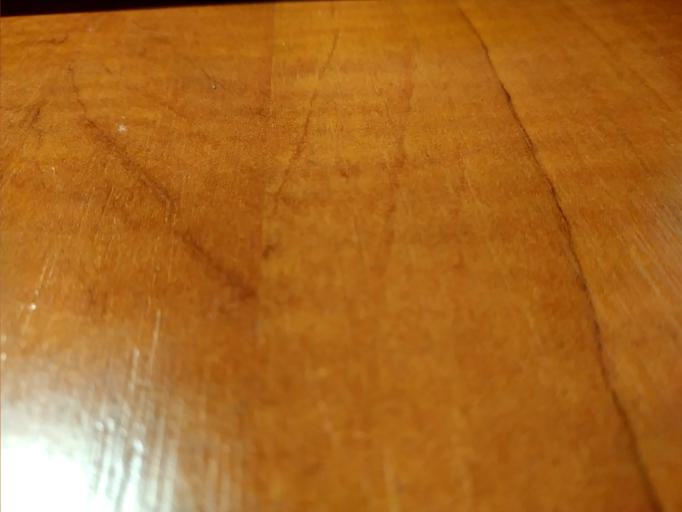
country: RU
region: Tverskaya
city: Ves'yegonsk
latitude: 58.8117
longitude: 37.5435
